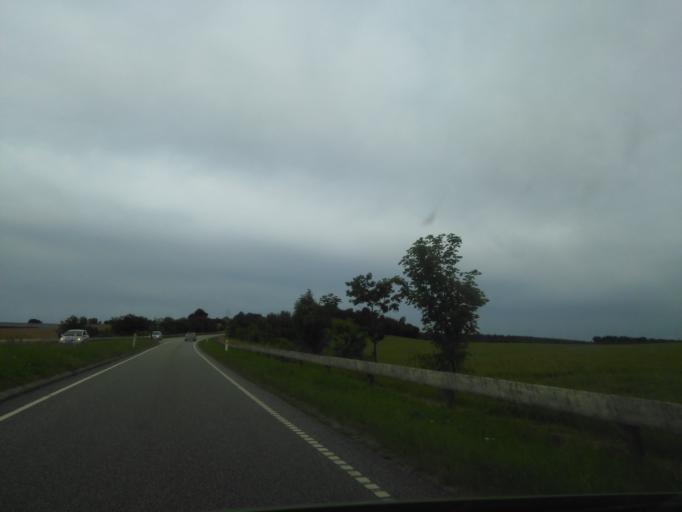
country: DK
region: Central Jutland
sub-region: Horsens Kommune
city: Horsens
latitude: 55.8956
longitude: 9.8750
